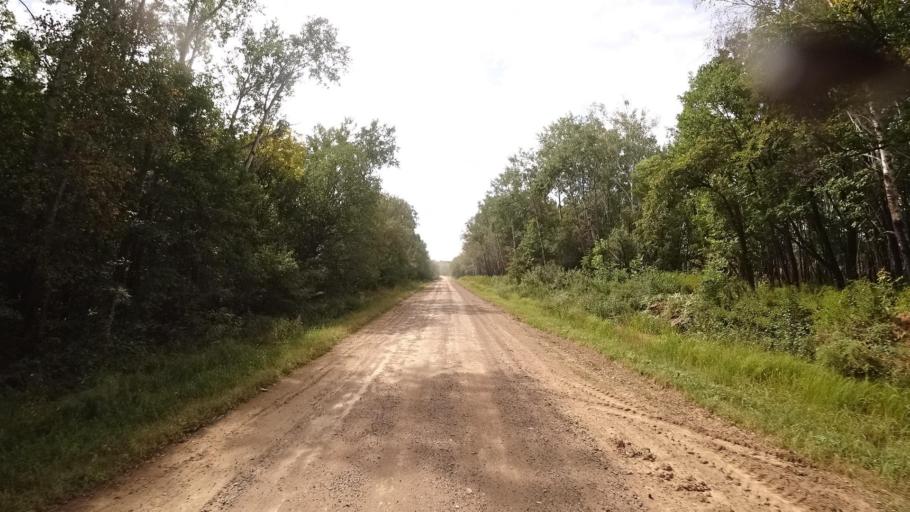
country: RU
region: Primorskiy
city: Yakovlevka
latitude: 44.5570
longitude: 133.5879
